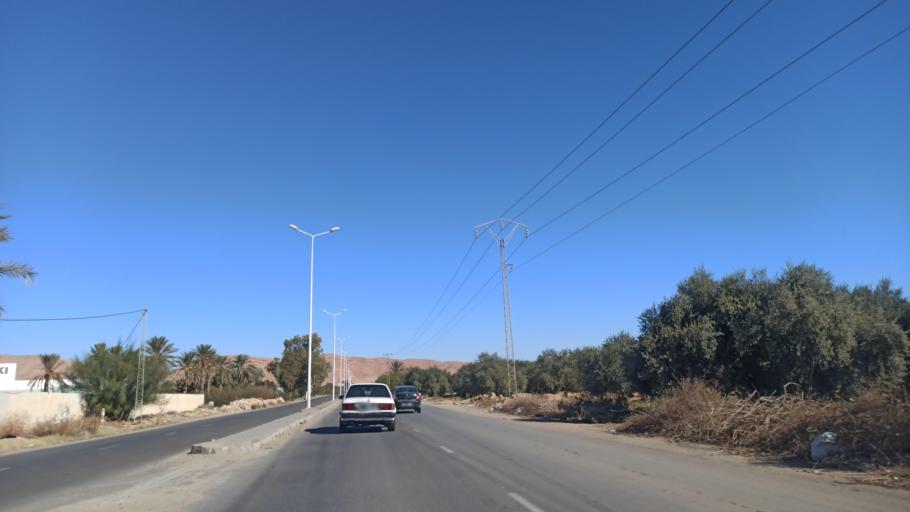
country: TN
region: Gafsa
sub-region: Gafsa Municipality
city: Gafsa
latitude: 34.4129
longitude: 8.7392
